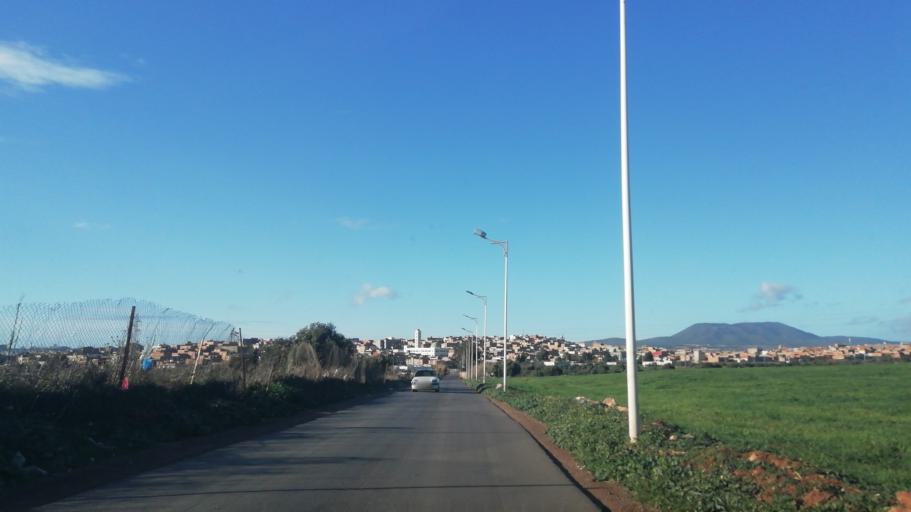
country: DZ
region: Oran
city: Sidi ech Chahmi
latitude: 35.6844
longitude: -0.4939
